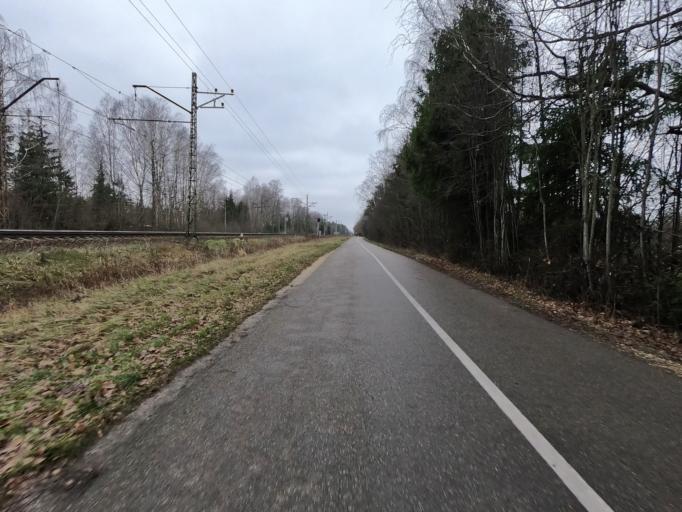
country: LV
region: Babite
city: Pinki
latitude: 56.9516
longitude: 23.9810
